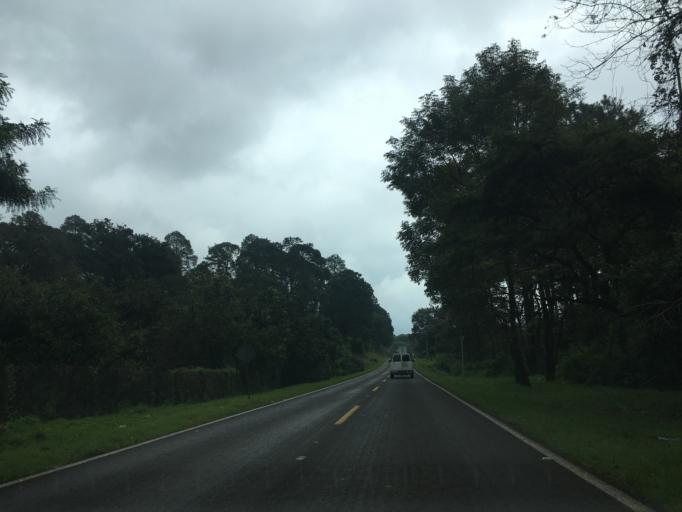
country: MX
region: Michoacan
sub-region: Uruapan
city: Toreo Bajo (El Toreo Bajo)
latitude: 19.4539
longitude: -101.9760
